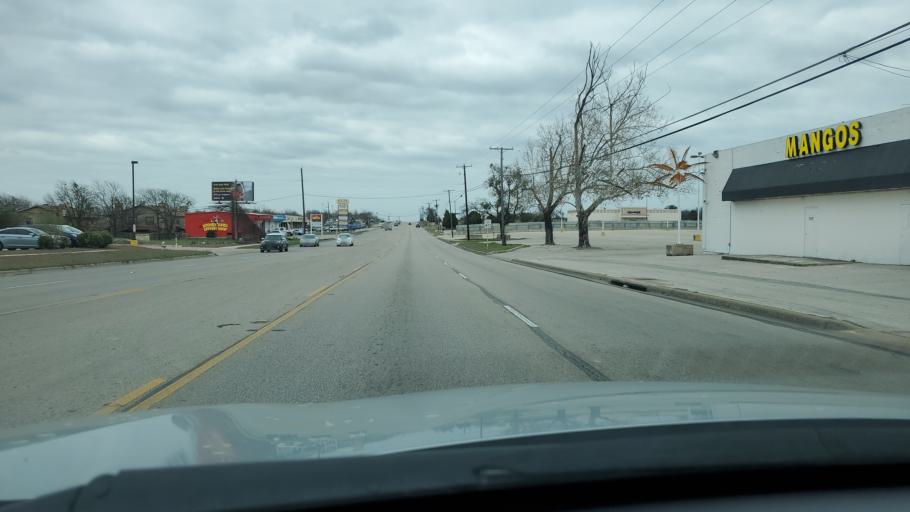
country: US
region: Texas
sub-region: Bell County
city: Killeen
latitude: 31.0859
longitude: -97.7541
